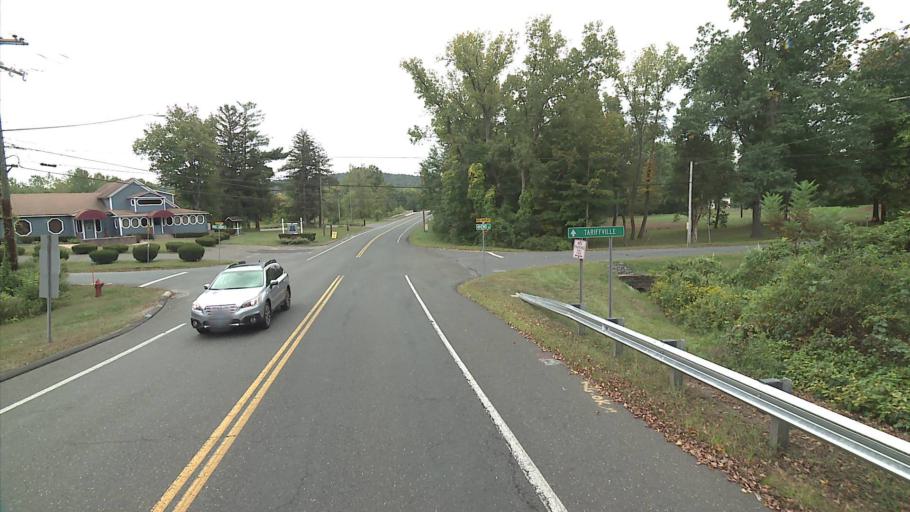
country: US
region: Connecticut
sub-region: Hartford County
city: Simsbury Center
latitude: 41.8957
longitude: -72.7864
